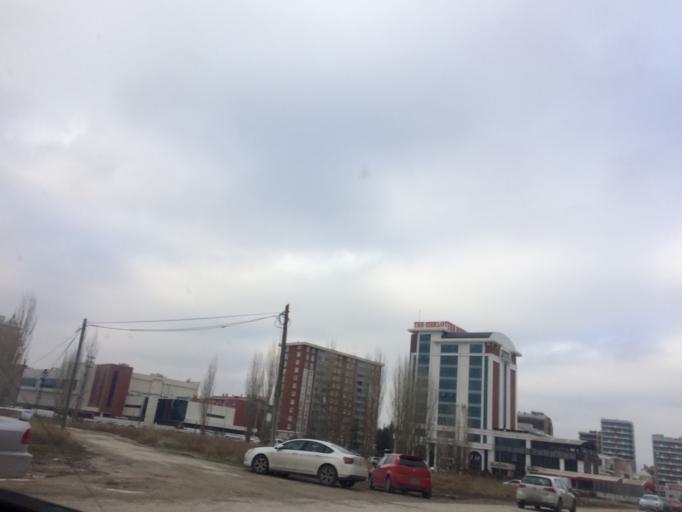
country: TR
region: Eskisehir
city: Eskisehir
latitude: 39.7814
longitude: 30.4986
